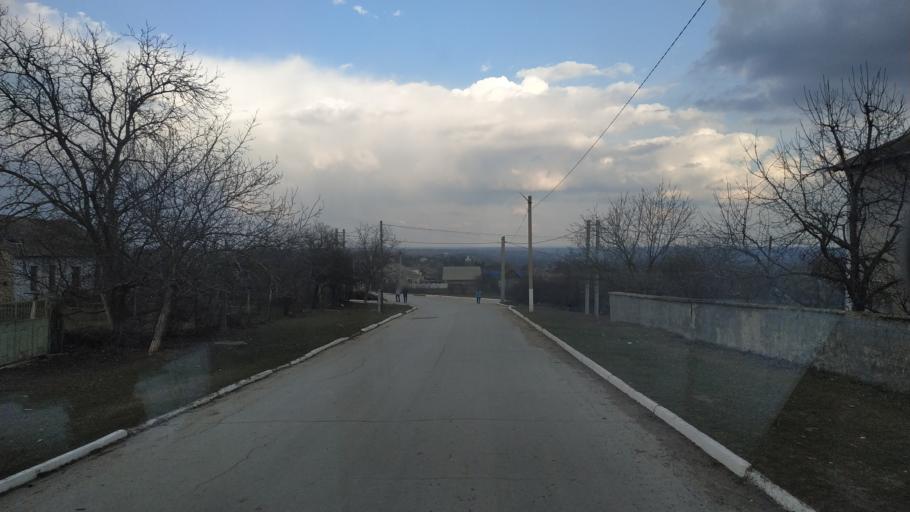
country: MD
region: Anenii Noi
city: Anenii Noi
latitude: 47.0034
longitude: 29.2914
